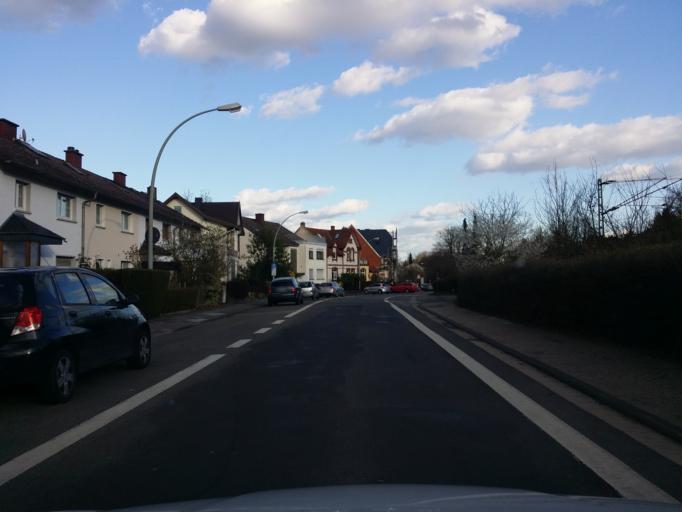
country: DE
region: Hesse
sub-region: Regierungsbezirk Darmstadt
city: Hofheim am Taunus
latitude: 50.0870
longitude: 8.4372
